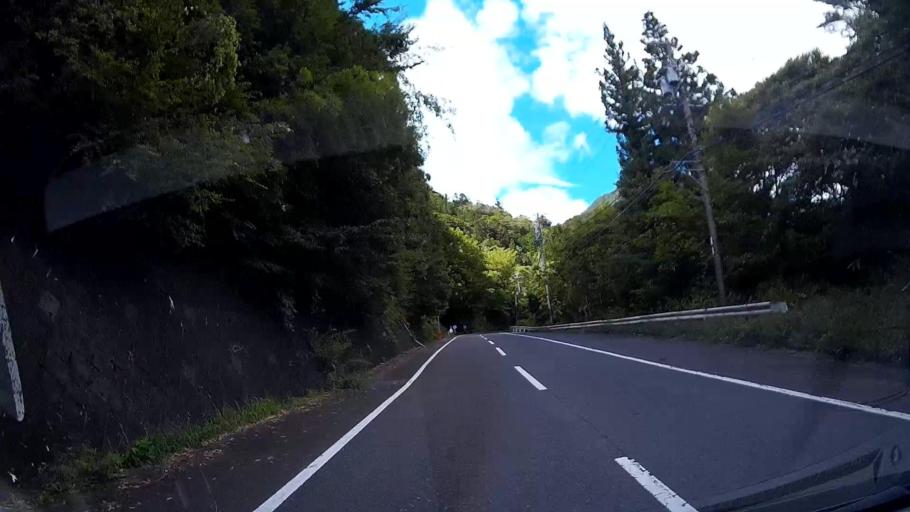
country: JP
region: Shizuoka
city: Shizuoka-shi
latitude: 35.2606
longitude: 138.2340
